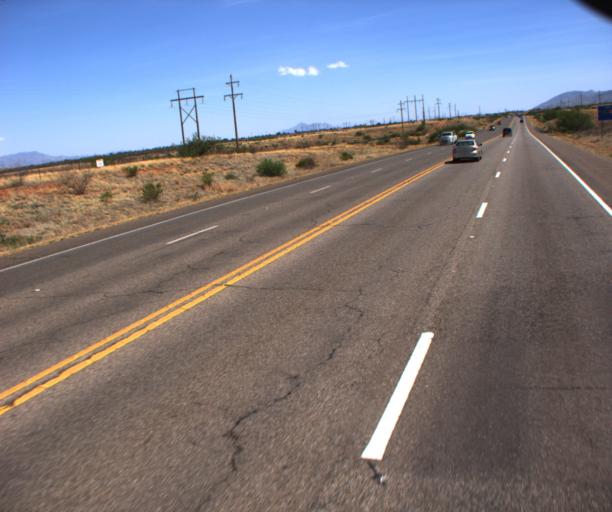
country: US
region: Arizona
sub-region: Cochise County
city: Sierra Vista
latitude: 31.5825
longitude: -110.3192
